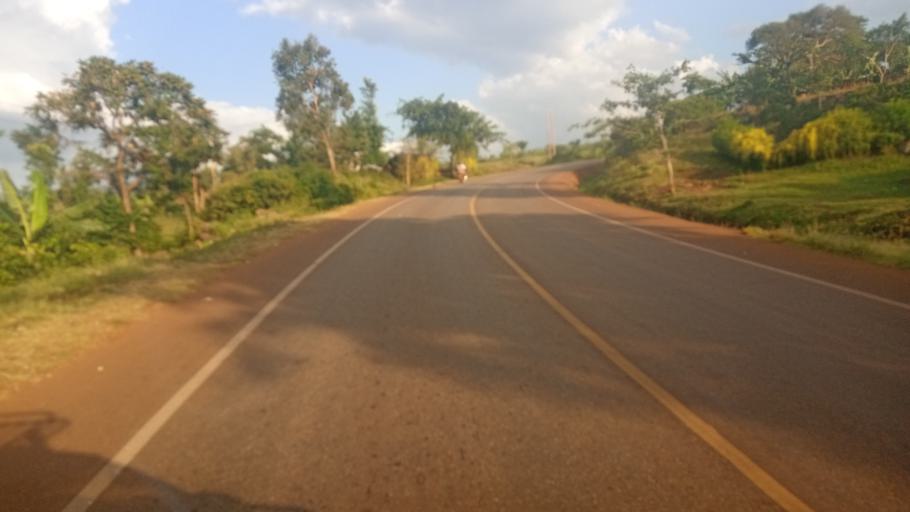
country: UG
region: Eastern Region
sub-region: Sironko District
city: Sironko
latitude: 1.3279
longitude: 34.3285
